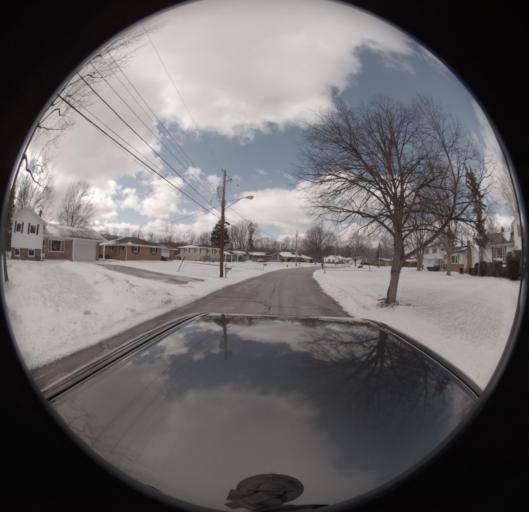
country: US
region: Ohio
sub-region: Lake County
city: Wickliffe
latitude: 41.6023
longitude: -81.4572
